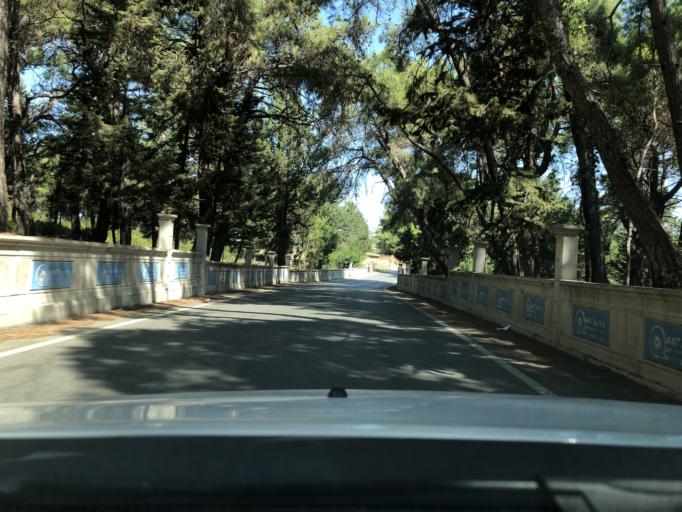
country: TR
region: Antalya
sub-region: Manavgat
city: Manavgat
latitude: 36.8157
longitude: 31.4890
